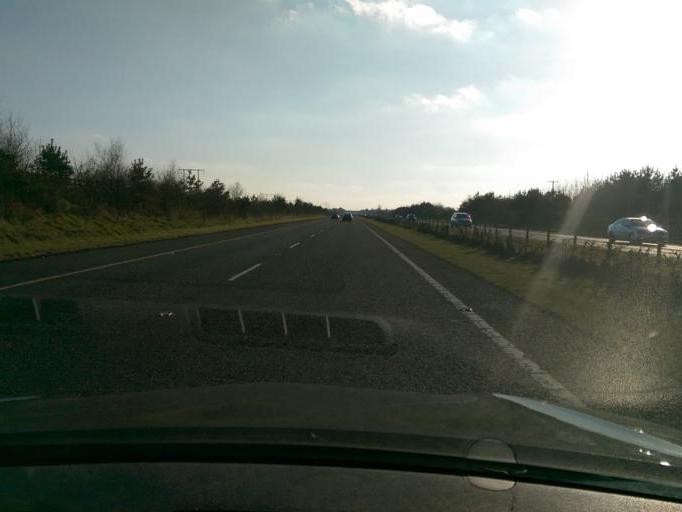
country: IE
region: Leinster
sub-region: Laois
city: Stradbally
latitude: 53.0760
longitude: -7.2028
